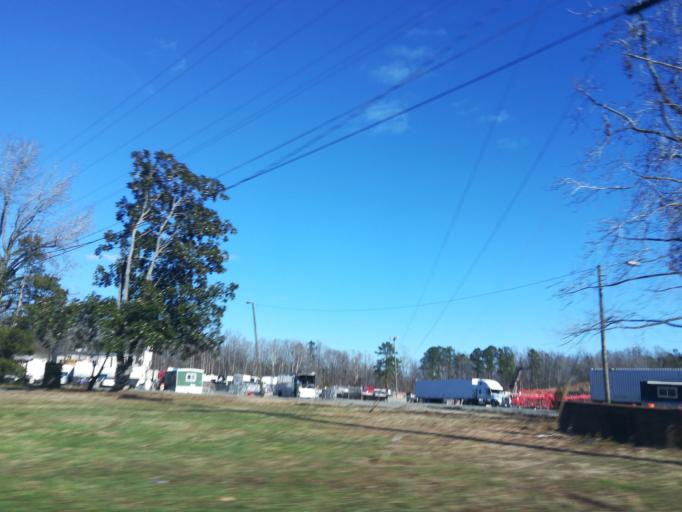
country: US
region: North Carolina
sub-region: Orange County
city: Hillsborough
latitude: 36.0355
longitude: -79.0049
